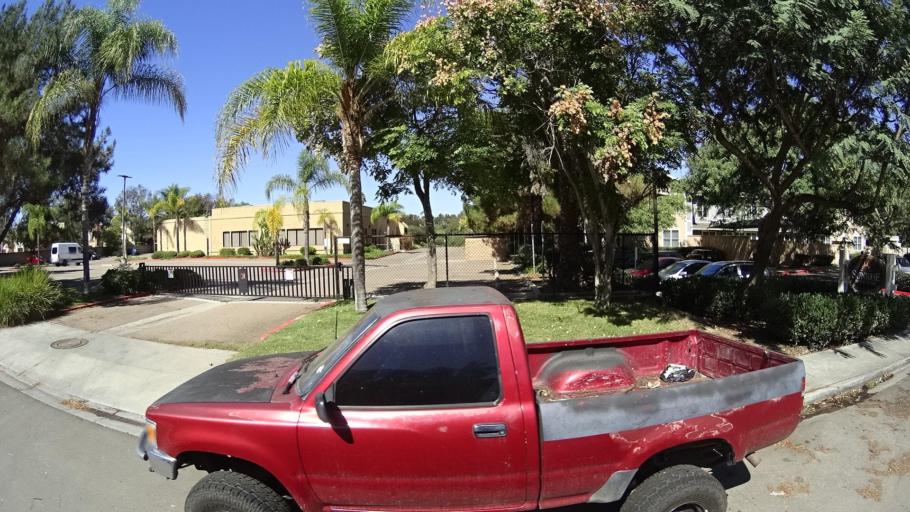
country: US
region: California
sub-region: San Diego County
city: Bonita
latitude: 32.6484
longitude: -117.0526
